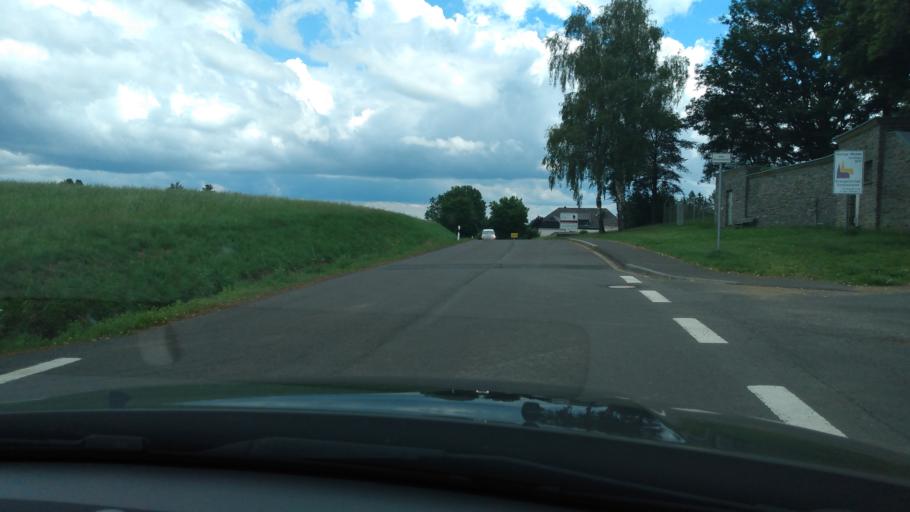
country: DE
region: Rheinland-Pfalz
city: Manderscheid
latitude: 50.0958
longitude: 6.8022
